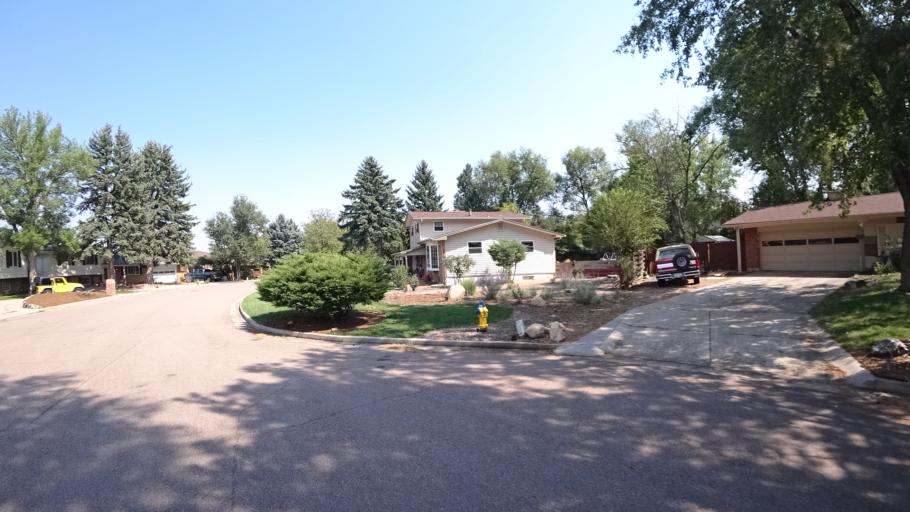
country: US
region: Colorado
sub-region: El Paso County
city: Colorado Springs
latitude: 38.8018
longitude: -104.8309
